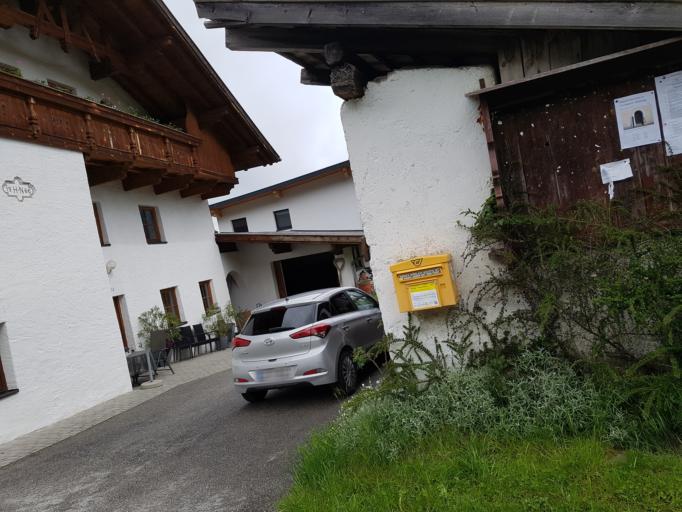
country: AT
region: Tyrol
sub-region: Politischer Bezirk Imst
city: Obsteig
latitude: 47.3085
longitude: 10.9447
